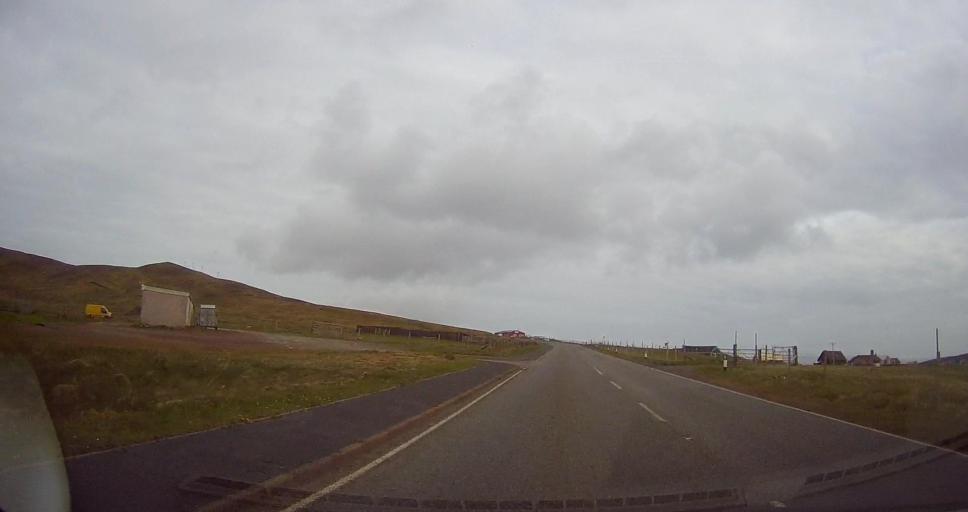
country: GB
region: Scotland
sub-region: Shetland Islands
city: Sandwick
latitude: 60.0586
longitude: -1.2234
